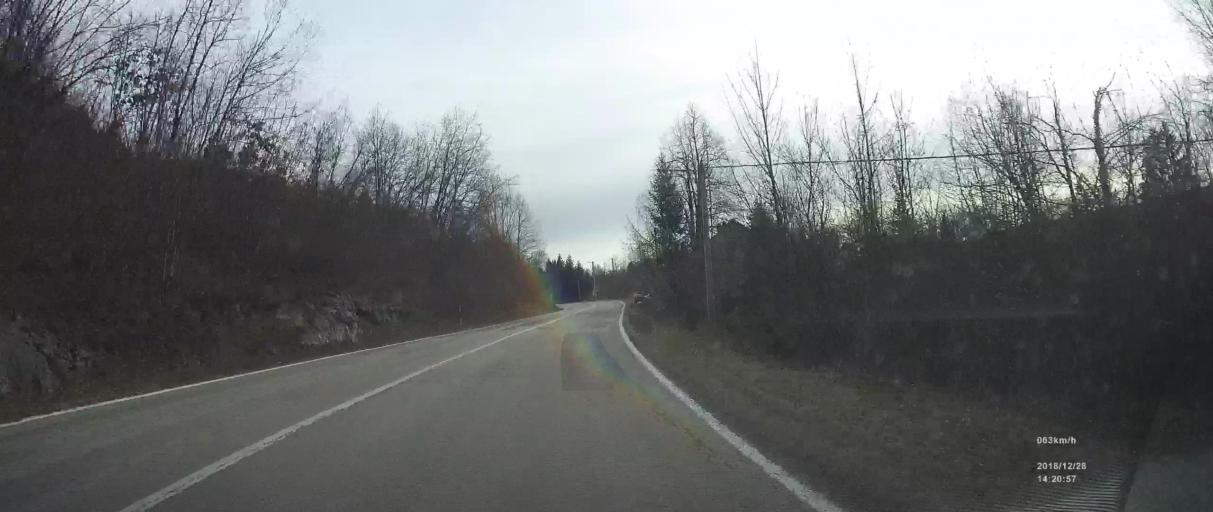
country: HR
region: Primorsko-Goranska
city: Vrbovsko
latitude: 45.3977
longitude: 15.0798
